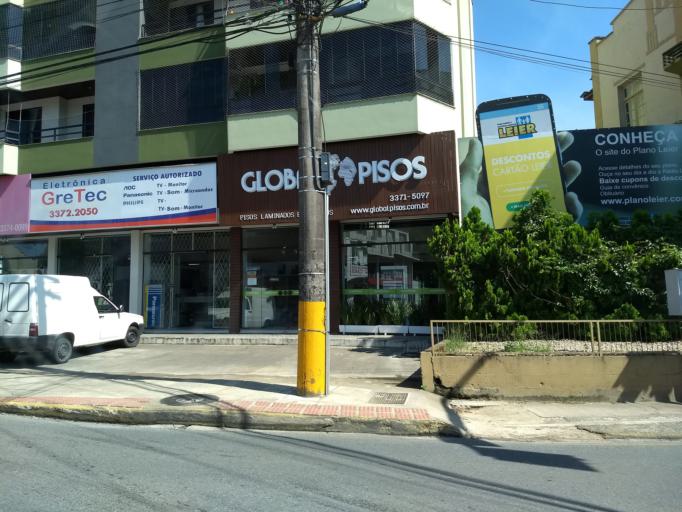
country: BR
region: Santa Catarina
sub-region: Jaragua Do Sul
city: Jaragua do Sul
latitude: -26.4952
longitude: -49.0882
